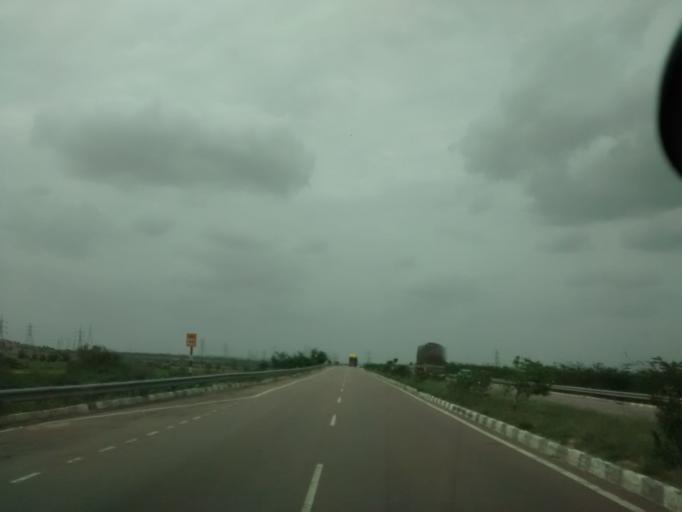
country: IN
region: Andhra Pradesh
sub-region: Kurnool
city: Ramapuram
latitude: 15.1296
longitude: 77.6610
